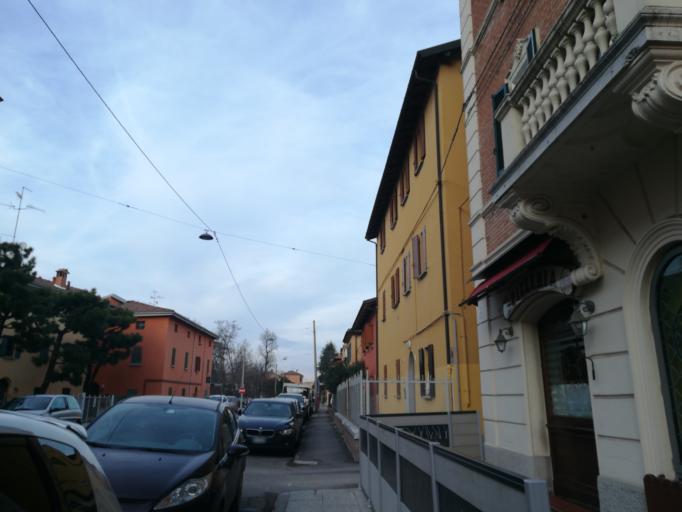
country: IT
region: Emilia-Romagna
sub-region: Provincia di Bologna
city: Progresso
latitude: 44.5462
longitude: 11.3539
